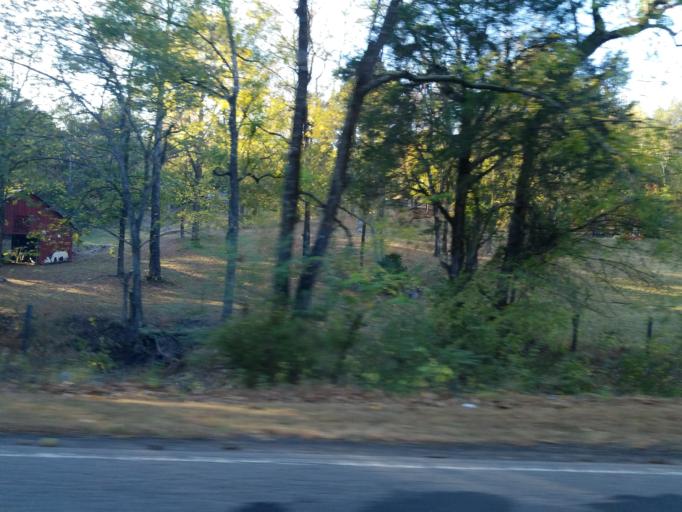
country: US
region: Georgia
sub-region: Bartow County
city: Adairsville
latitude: 34.2867
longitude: -84.9432
